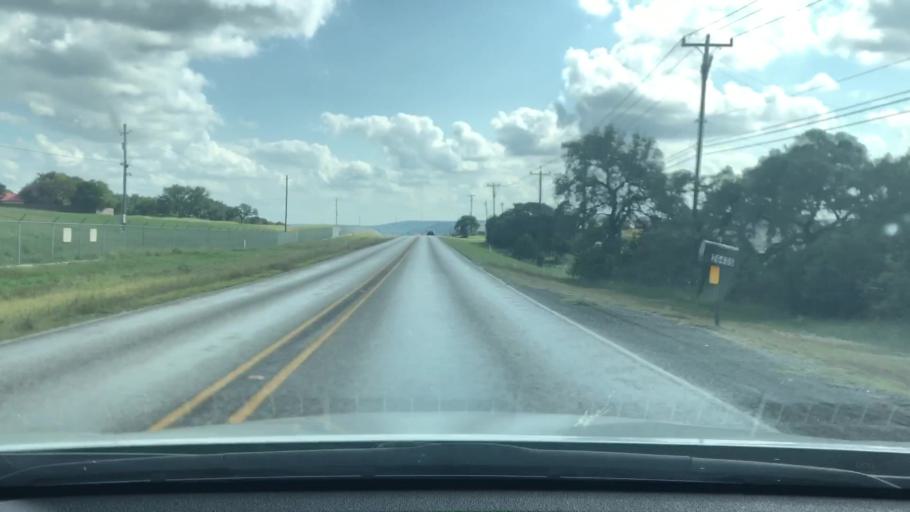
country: US
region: Texas
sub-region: Bexar County
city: Scenic Oaks
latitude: 29.6929
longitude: -98.6315
